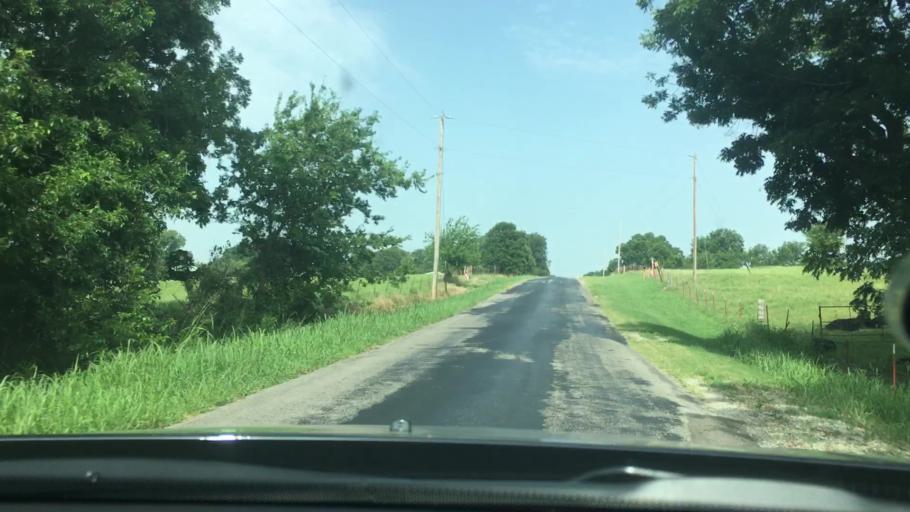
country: US
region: Oklahoma
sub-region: Garvin County
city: Pauls Valley
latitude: 34.8258
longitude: -97.2024
